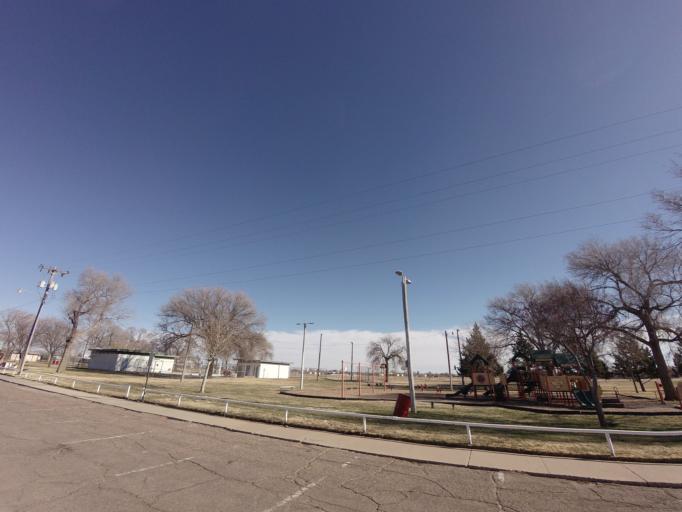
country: US
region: New Mexico
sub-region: Curry County
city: Clovis
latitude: 34.4019
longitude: -103.2306
